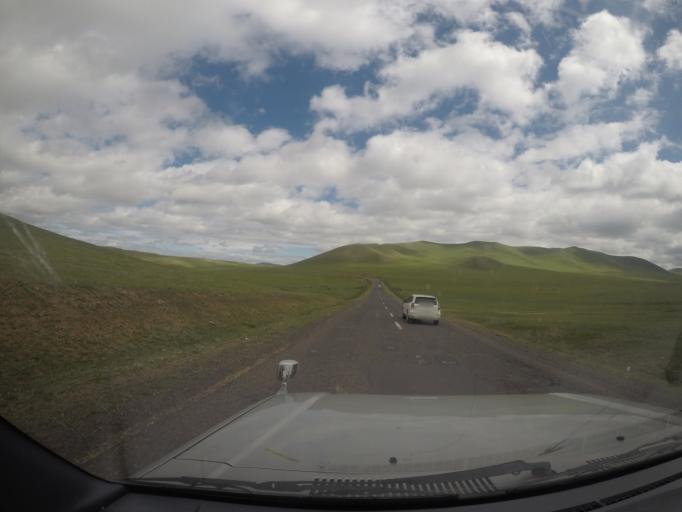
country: MN
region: Hentiy
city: Modot
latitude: 47.7542
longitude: 108.9393
